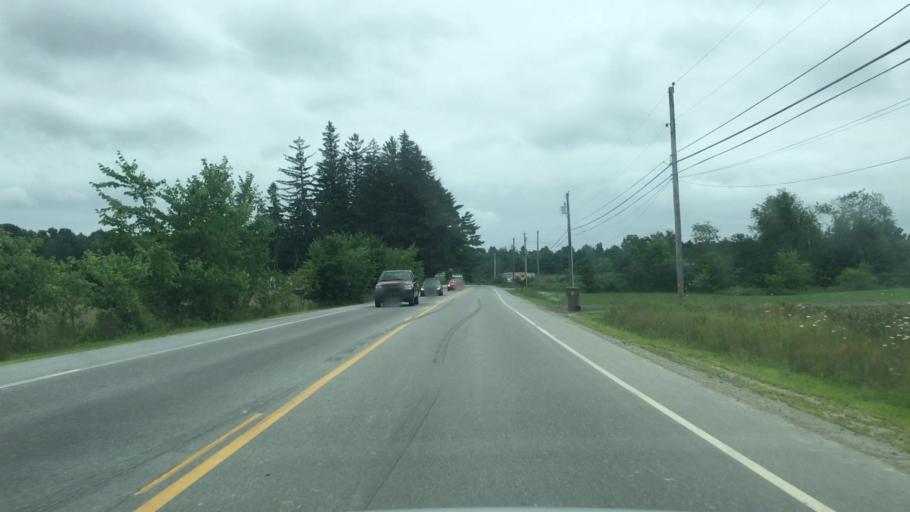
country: US
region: Maine
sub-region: York County
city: Biddeford
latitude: 43.5191
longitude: -70.4822
